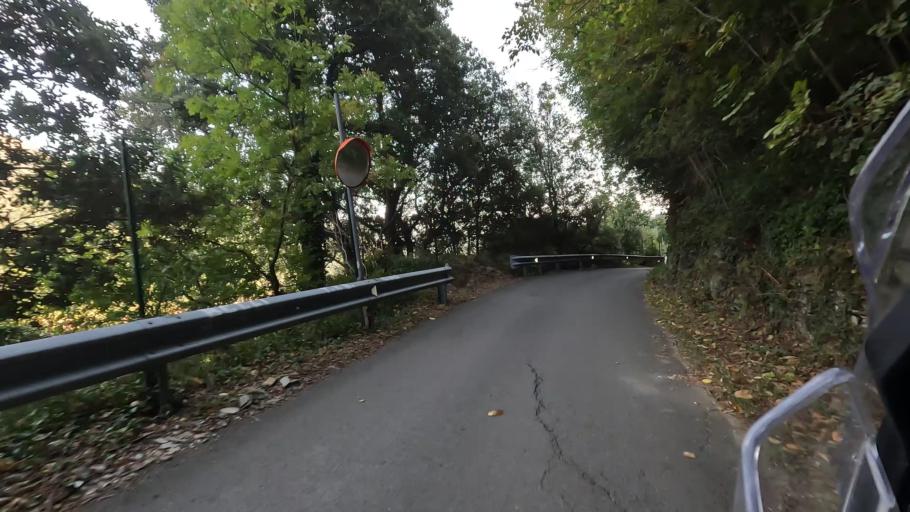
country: IT
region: Liguria
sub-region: Provincia di Savona
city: San Giovanni
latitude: 44.3989
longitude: 8.5340
